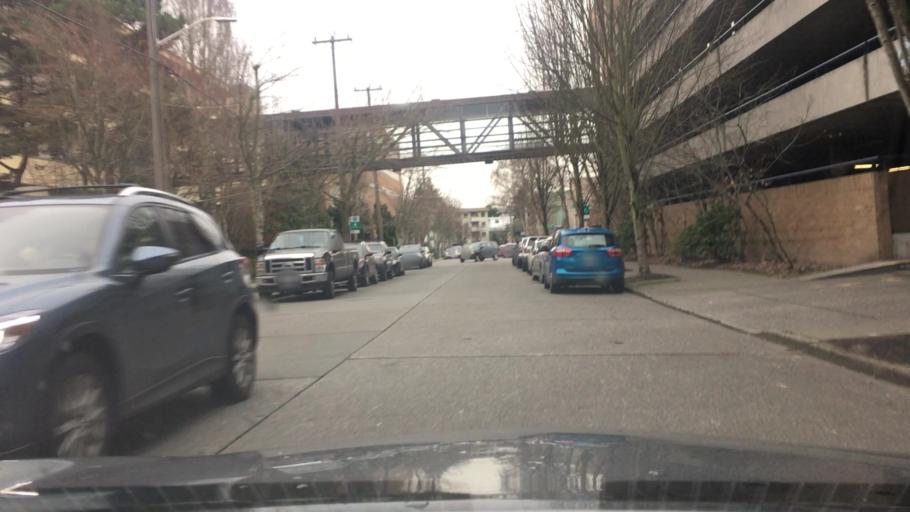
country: US
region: Washington
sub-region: King County
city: Seattle
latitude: 47.6678
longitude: -122.3807
